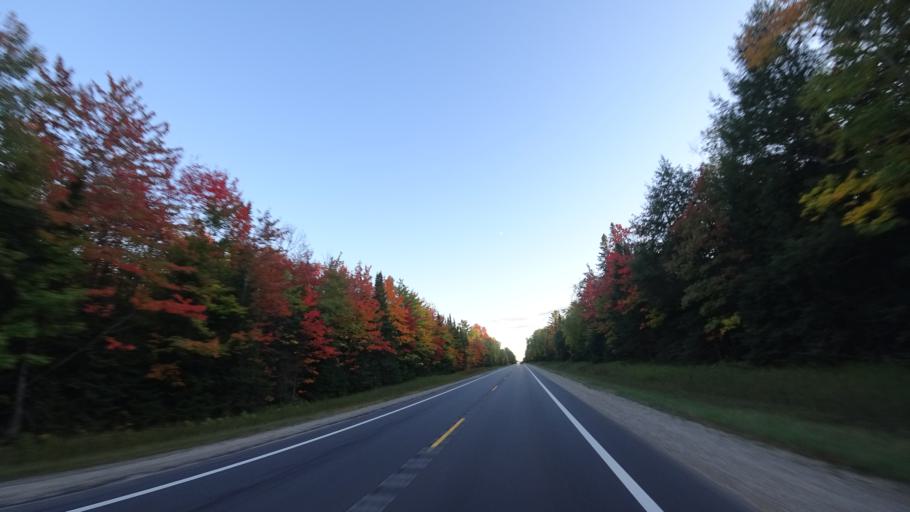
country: US
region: Michigan
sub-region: Mackinac County
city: Saint Ignace
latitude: 46.2723
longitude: -85.0095
